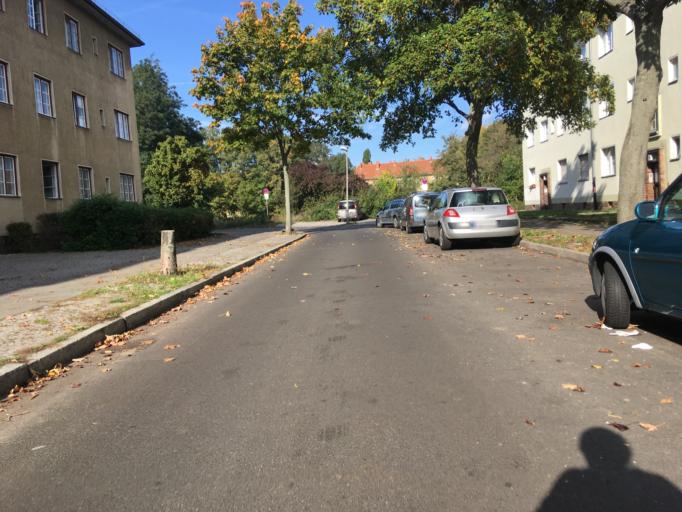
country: DE
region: Berlin
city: Wilhelmsruh
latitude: 52.5720
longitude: 13.3631
